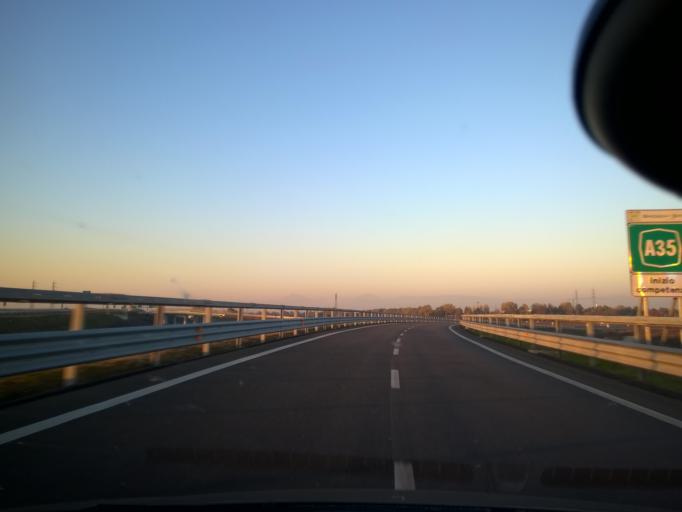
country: IT
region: Lombardy
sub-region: Citta metropolitana di Milano
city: Pozzuolo Martesana
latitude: 45.5020
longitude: 9.4449
